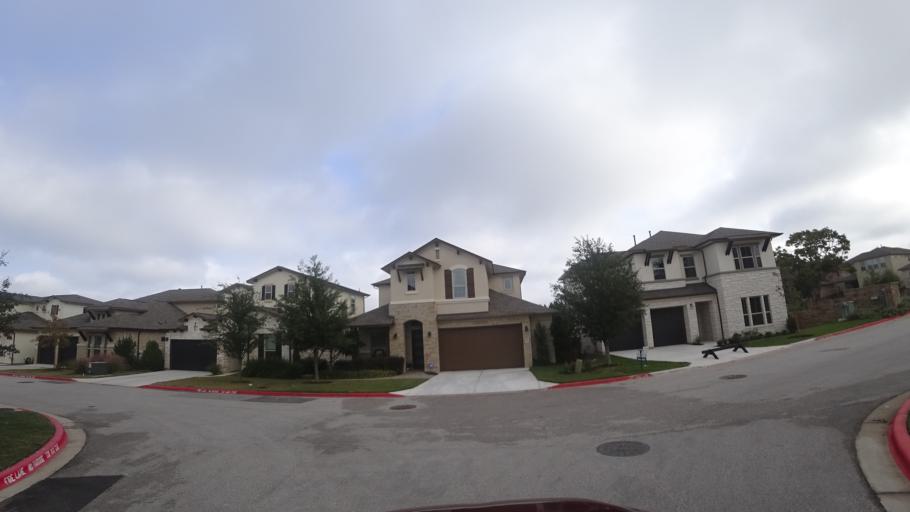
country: US
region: Texas
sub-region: Williamson County
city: Anderson Mill
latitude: 30.4003
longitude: -97.8446
